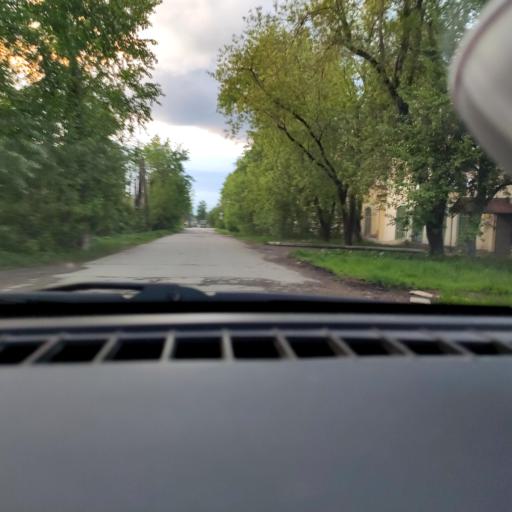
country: RU
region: Perm
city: Perm
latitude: 58.0867
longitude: 56.3855
